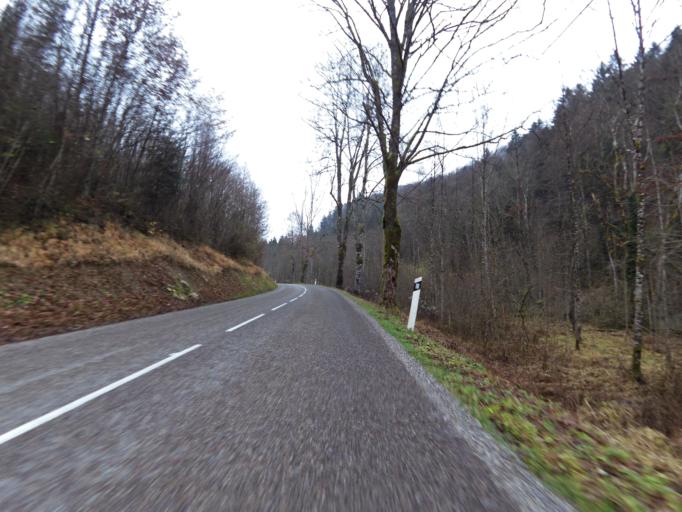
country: FR
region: Alsace
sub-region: Departement du Haut-Rhin
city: Ferrette
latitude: 47.4383
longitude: 7.3110
